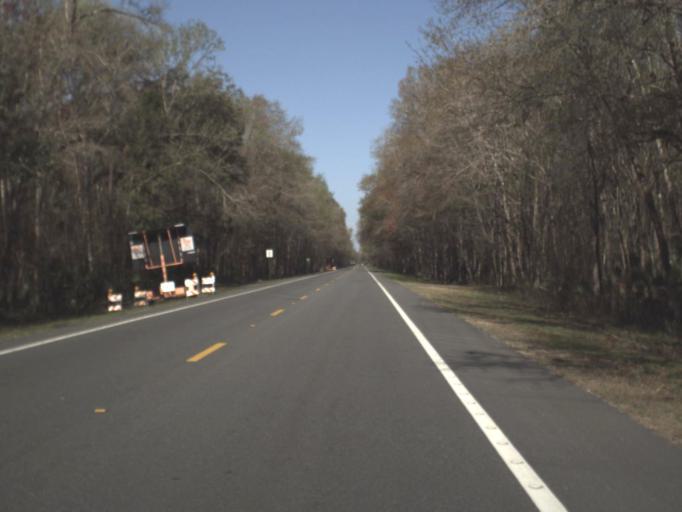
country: US
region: Florida
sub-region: Leon County
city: Woodville
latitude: 30.1506
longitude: -83.9825
